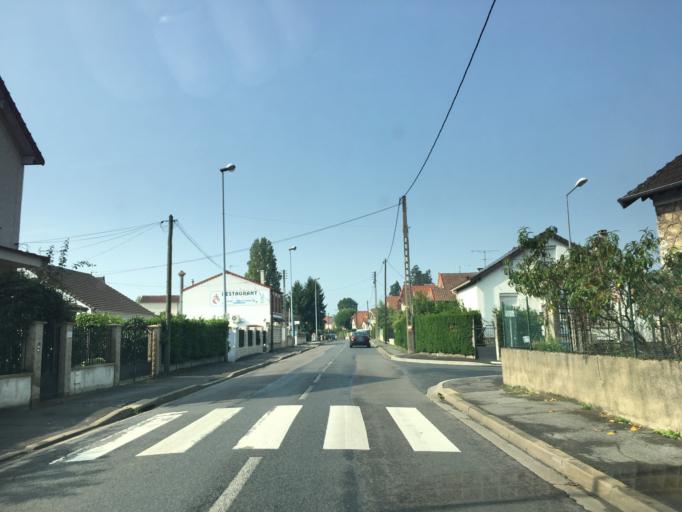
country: FR
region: Ile-de-France
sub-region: Departement du Val-de-Marne
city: Boissy-Saint-Leger
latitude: 48.7524
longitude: 2.5202
